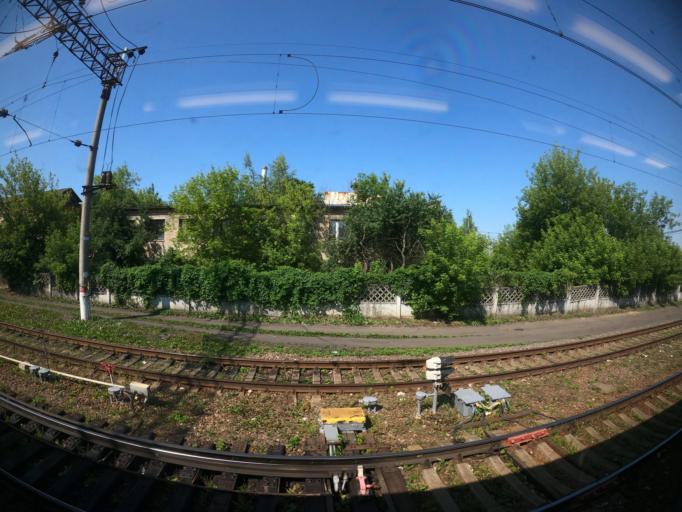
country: RU
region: Moskovskaya
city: Serpukhov
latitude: 54.9397
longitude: 37.4515
